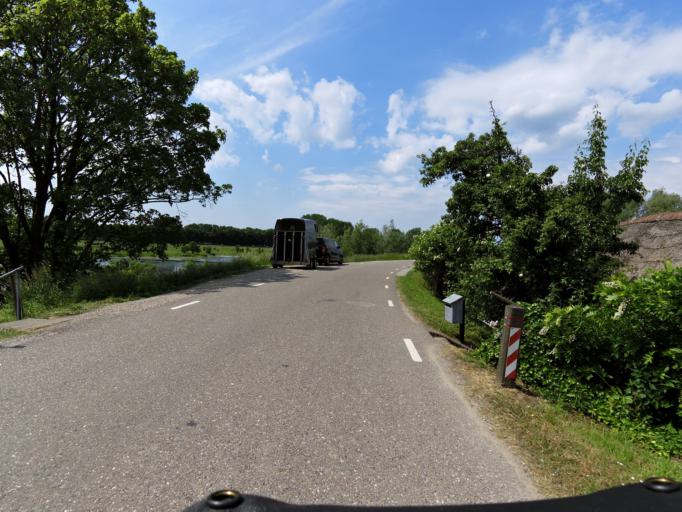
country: NL
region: North Brabant
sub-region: Gemeente Woudrichem
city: Woudrichem
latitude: 51.7921
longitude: 5.0570
